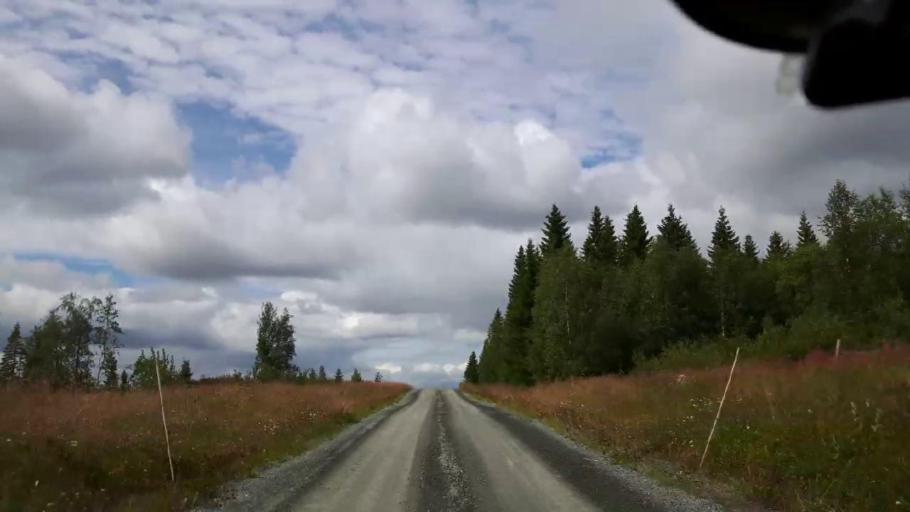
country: SE
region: Jaemtland
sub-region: Krokoms Kommun
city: Valla
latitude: 63.5719
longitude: 13.9143
